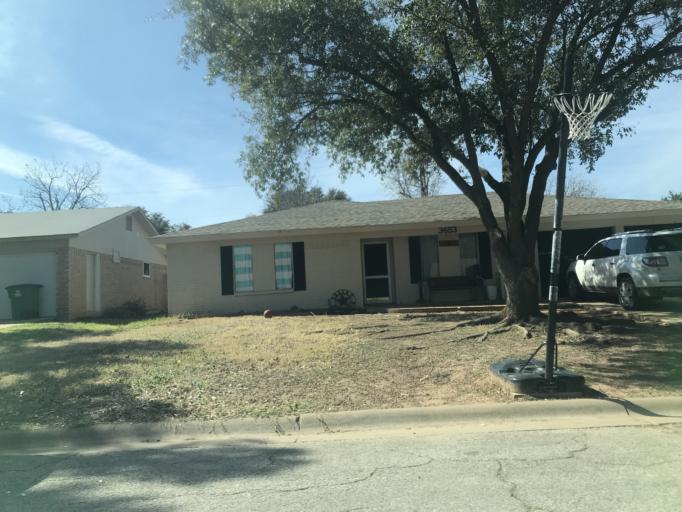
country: US
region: Texas
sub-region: Tom Green County
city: San Angelo
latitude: 31.4337
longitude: -100.4870
